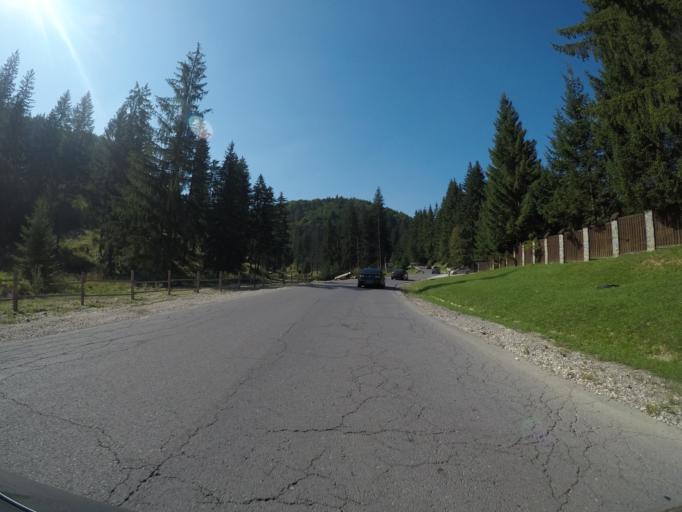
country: RO
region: Brasov
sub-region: Comuna Cristian
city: Cristian
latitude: 45.5901
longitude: 25.5259
